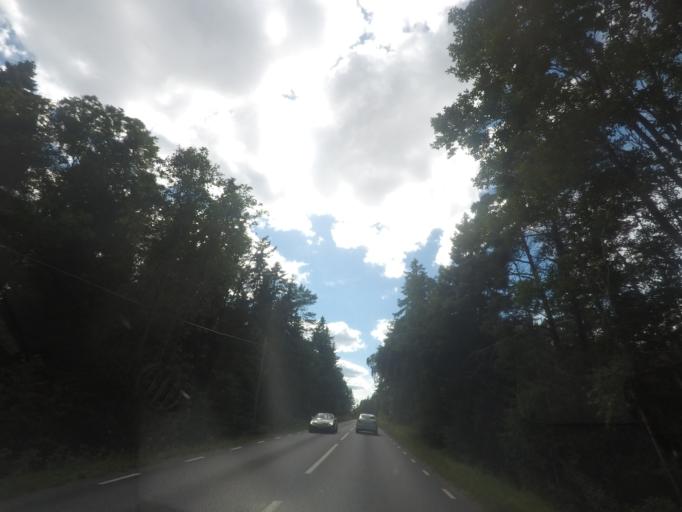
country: SE
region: Stockholm
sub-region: Norrtalje Kommun
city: Arno
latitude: 60.0948
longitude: 18.7995
